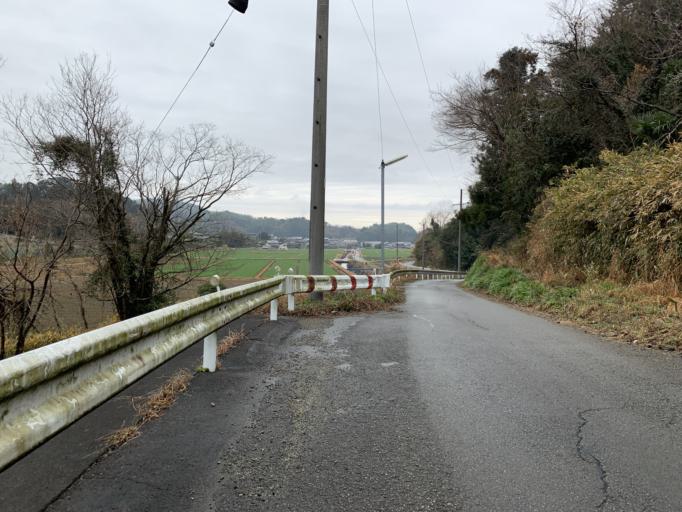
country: JP
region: Mie
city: Ise
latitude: 34.4725
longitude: 136.5469
